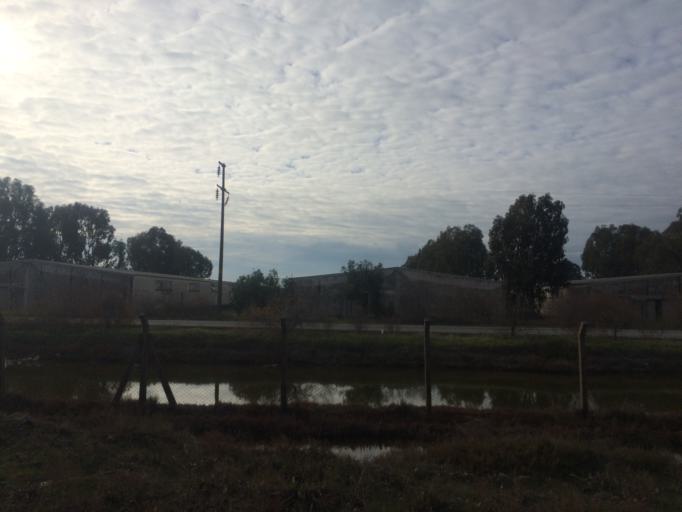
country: TR
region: Izmir
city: Menemen
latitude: 38.4933
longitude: 26.9437
